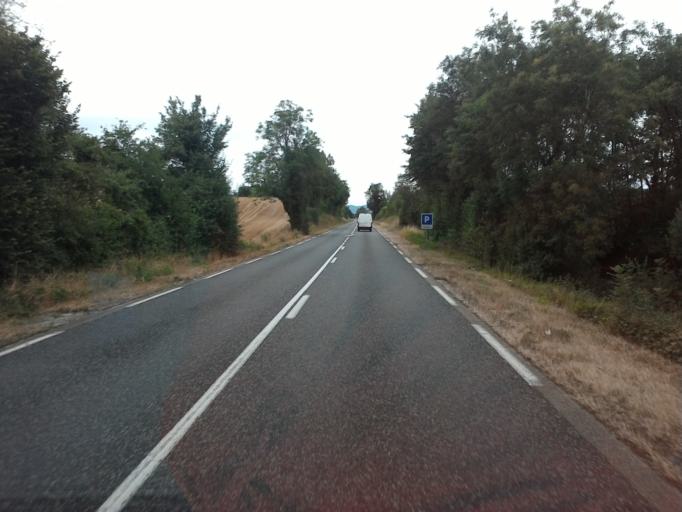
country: FR
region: Rhone-Alpes
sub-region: Departement de l'Isere
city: Bouvesse-Quirieu
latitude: 45.7593
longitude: 5.4032
